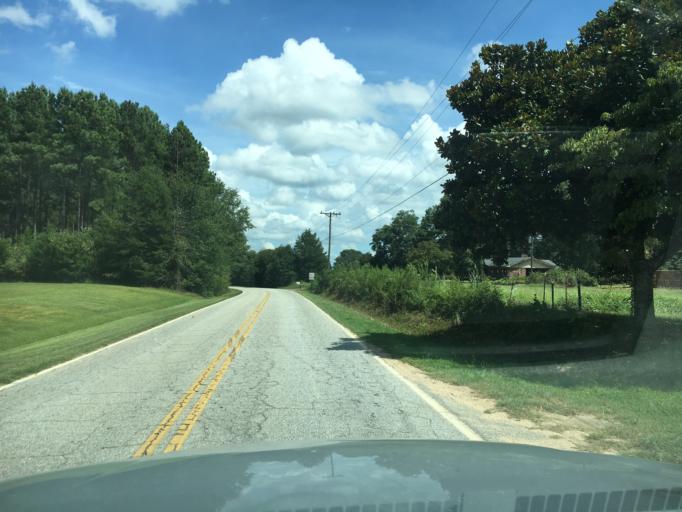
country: US
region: South Carolina
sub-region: Anderson County
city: Belton
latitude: 34.5651
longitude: -82.4769
